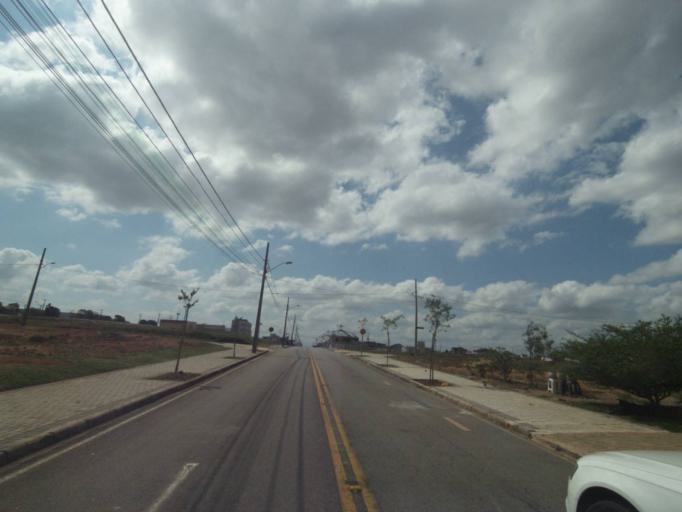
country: BR
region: Parana
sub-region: Curitiba
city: Curitiba
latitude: -25.5080
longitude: -49.3111
